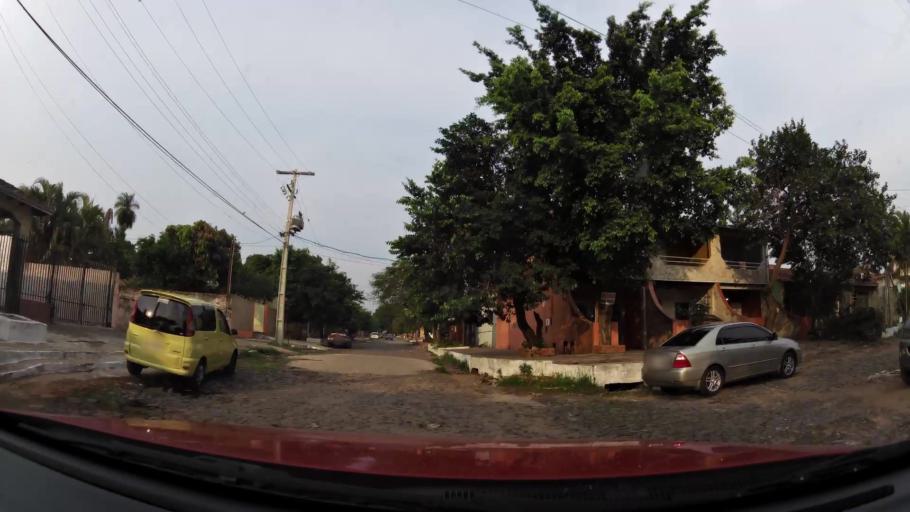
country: PY
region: Central
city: Lambare
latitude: -25.3271
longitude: -57.5796
